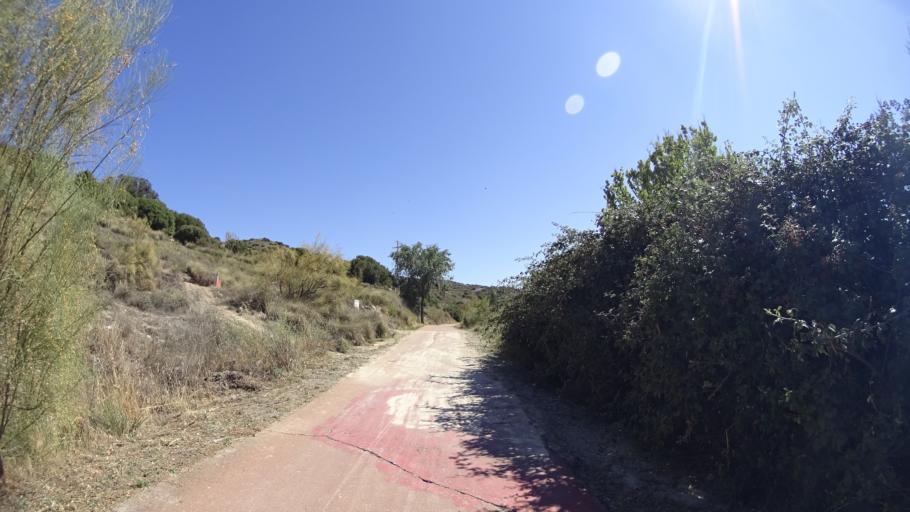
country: ES
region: Madrid
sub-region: Provincia de Madrid
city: Morata de Tajuna
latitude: 40.2312
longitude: -3.3998
